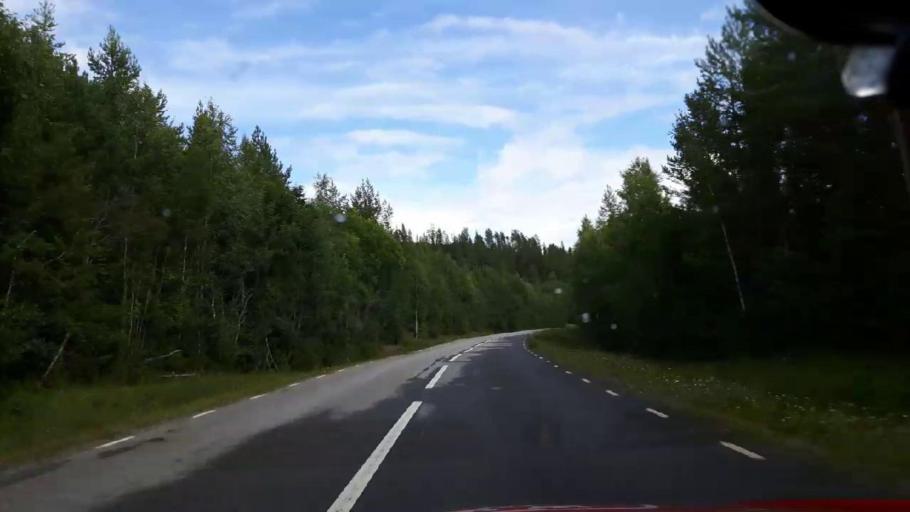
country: SE
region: Jaemtland
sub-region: Stroemsunds Kommun
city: Stroemsund
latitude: 64.3465
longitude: 15.0515
